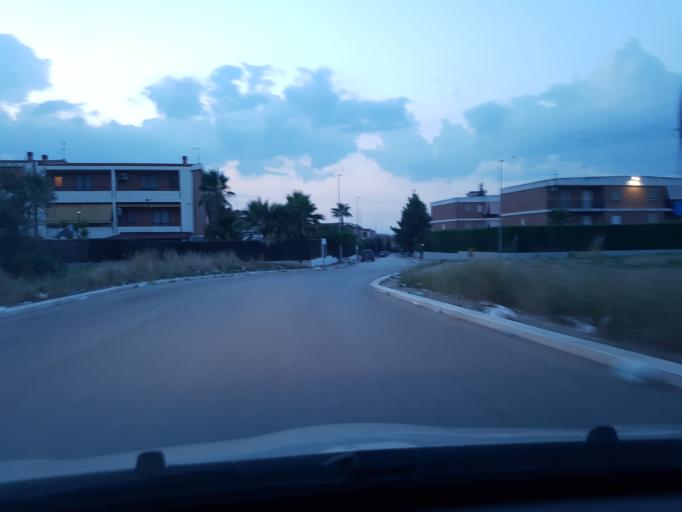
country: IT
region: Apulia
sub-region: Provincia di Foggia
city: Cerignola
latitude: 41.2597
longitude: 15.8805
